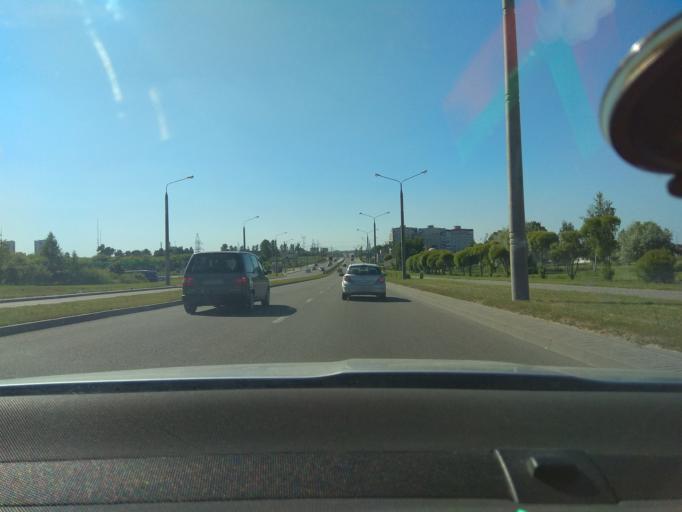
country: BY
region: Grodnenskaya
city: Hrodna
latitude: 53.6488
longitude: 23.8064
